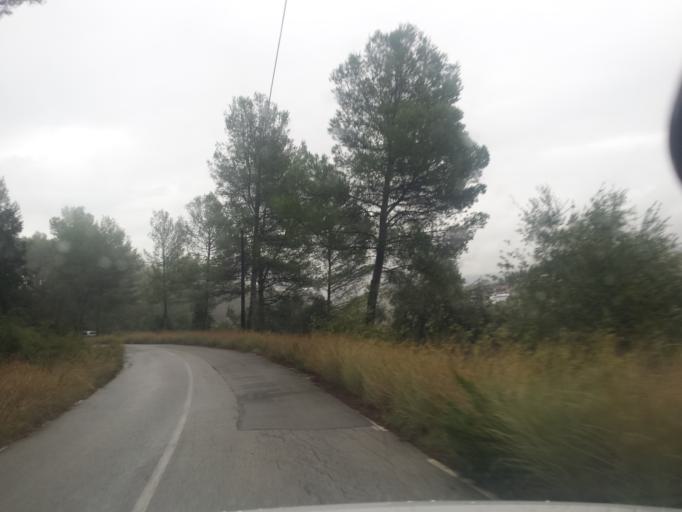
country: ES
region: Catalonia
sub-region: Provincia de Barcelona
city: Sant Andreu de la Barca
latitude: 41.4364
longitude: 1.9453
